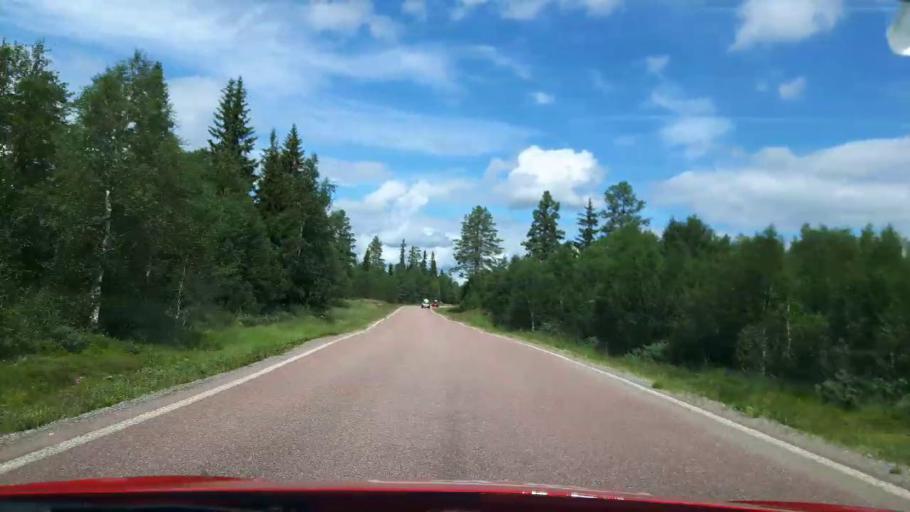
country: NO
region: Hedmark
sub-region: Trysil
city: Innbygda
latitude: 62.0152
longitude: 12.9777
